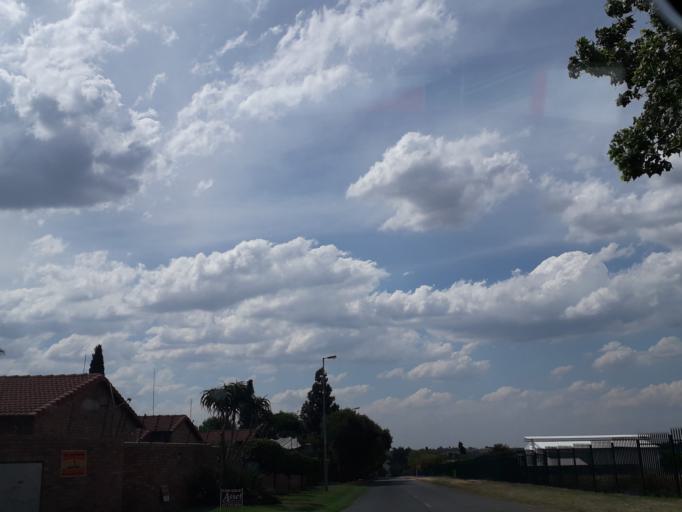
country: ZA
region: Gauteng
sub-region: City of Johannesburg Metropolitan Municipality
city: Roodepoort
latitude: -26.0967
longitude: 27.9064
